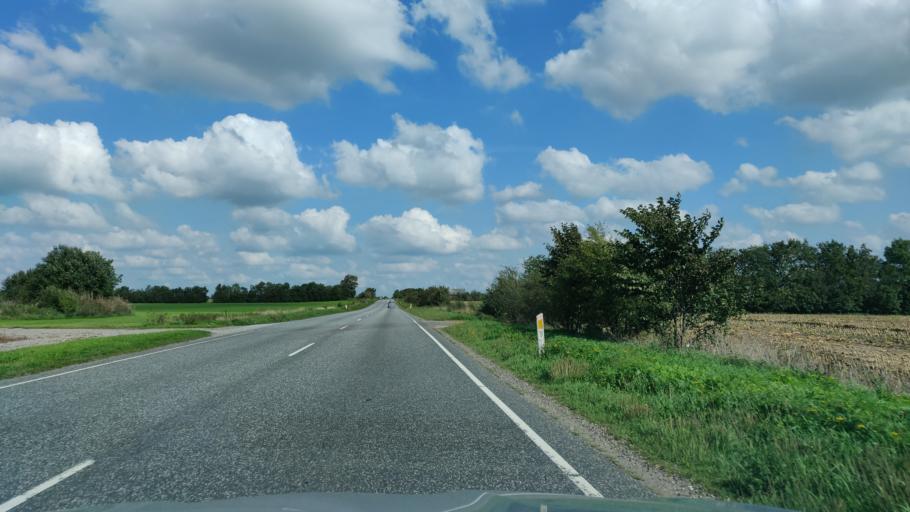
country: DK
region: North Denmark
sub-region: Vesthimmerland Kommune
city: Aars
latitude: 56.7747
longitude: 9.5734
